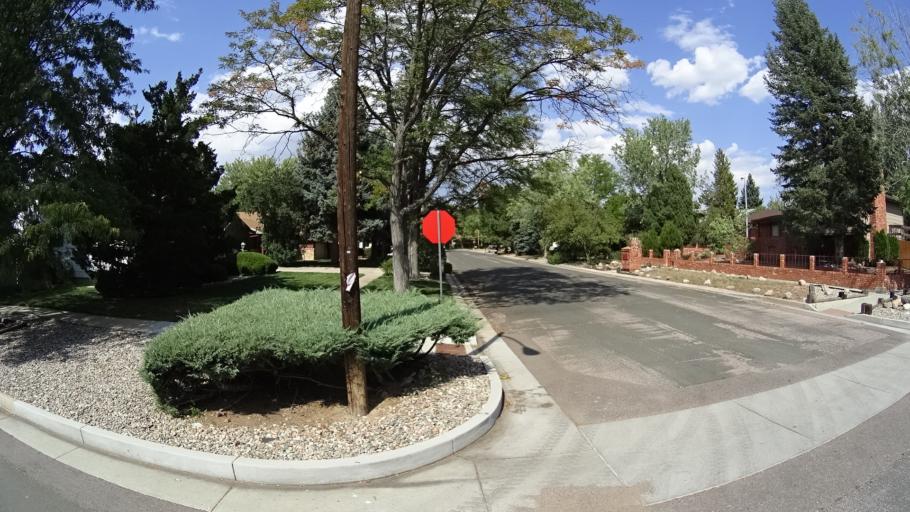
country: US
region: Colorado
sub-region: El Paso County
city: Colorado Springs
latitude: 38.8485
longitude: -104.7625
